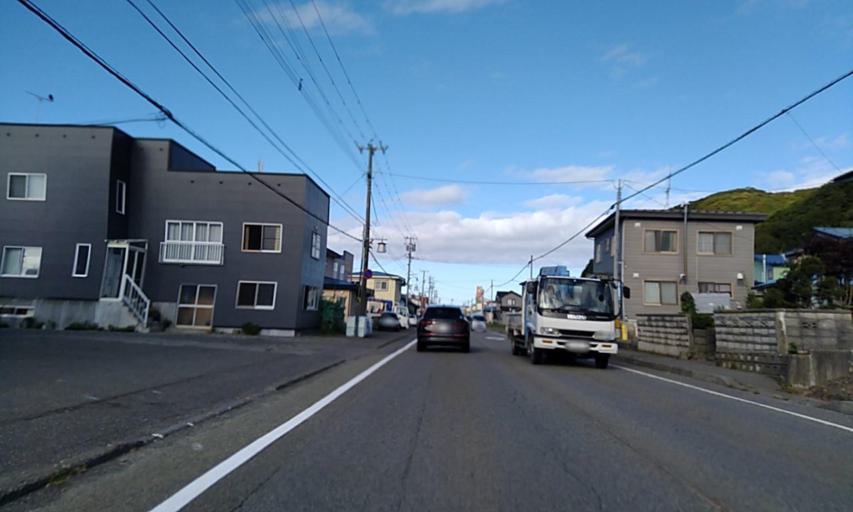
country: JP
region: Hokkaido
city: Shizunai-furukawacho
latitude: 42.2508
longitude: 142.5486
